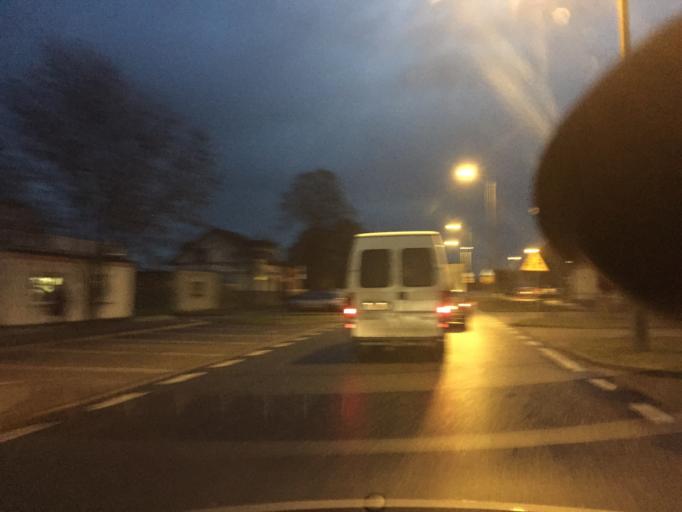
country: PL
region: Kujawsko-Pomorskie
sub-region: Powiat golubsko-dobrzynski
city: Kowalewo Pomorskie
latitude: 53.1531
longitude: 18.8977
